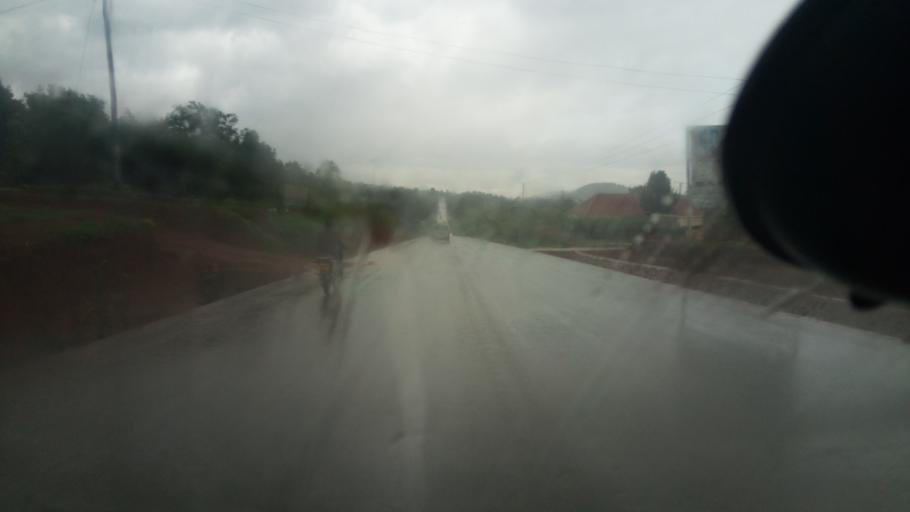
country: UG
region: Central Region
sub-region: Wakiso District
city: Wakiso
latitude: 0.4095
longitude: 32.4645
